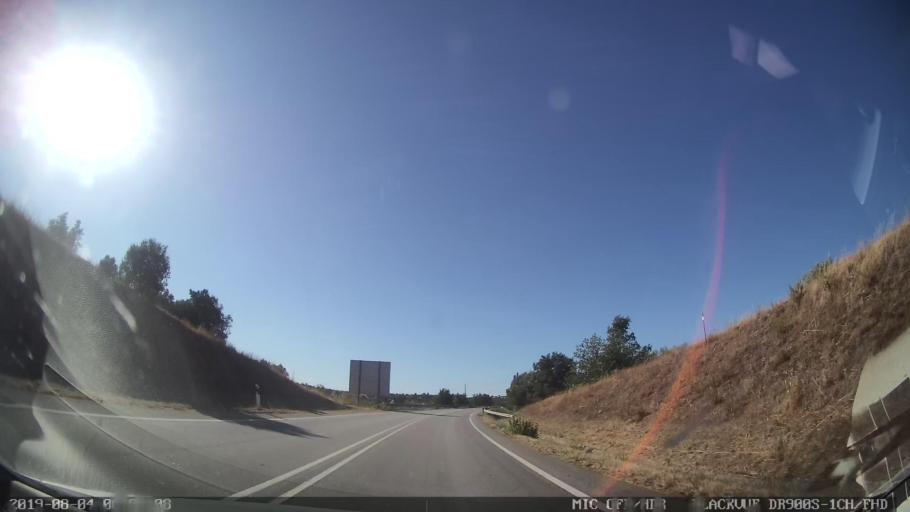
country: PT
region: Santarem
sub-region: Abrantes
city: Alferrarede
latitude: 39.4876
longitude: -8.0983
